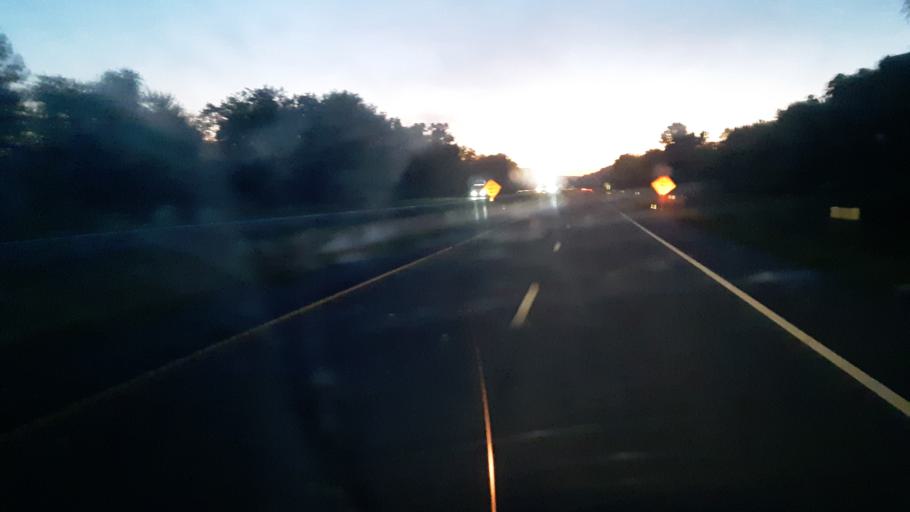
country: US
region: New York
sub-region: Montgomery County
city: Fonda
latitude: 42.9246
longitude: -74.4274
